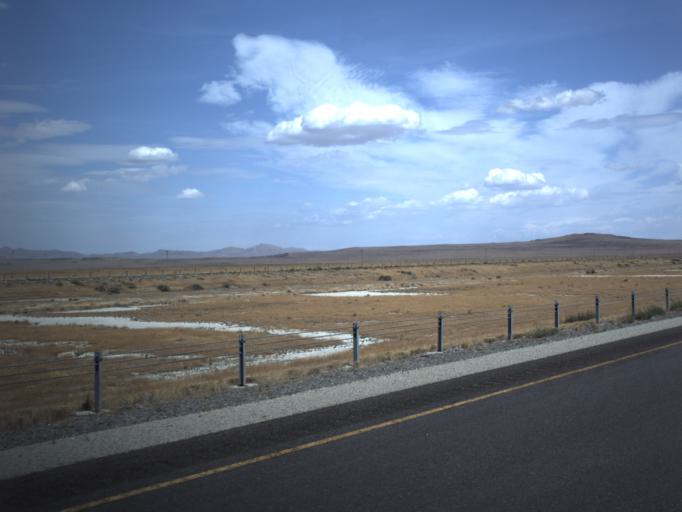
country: US
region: Utah
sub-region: Tooele County
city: Grantsville
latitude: 40.7260
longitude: -113.2218
